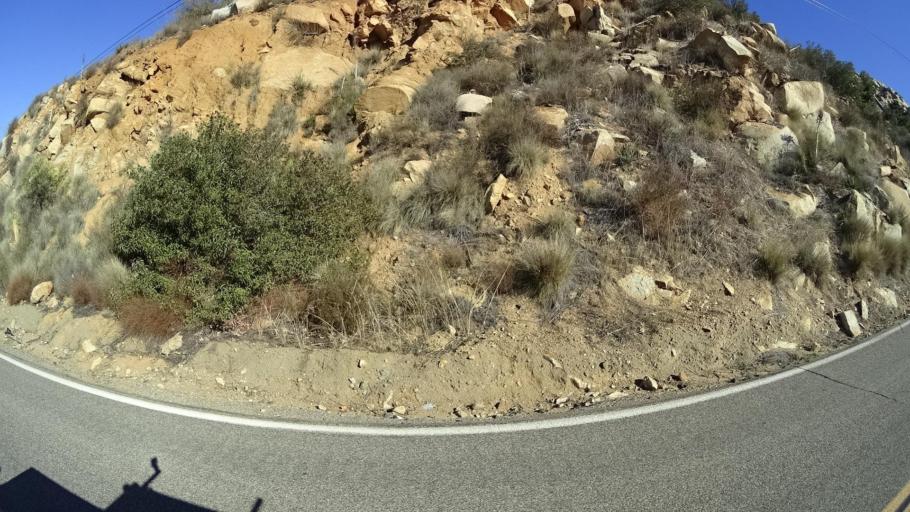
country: US
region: California
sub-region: San Diego County
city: Jamul
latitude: 32.6727
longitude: -116.7664
